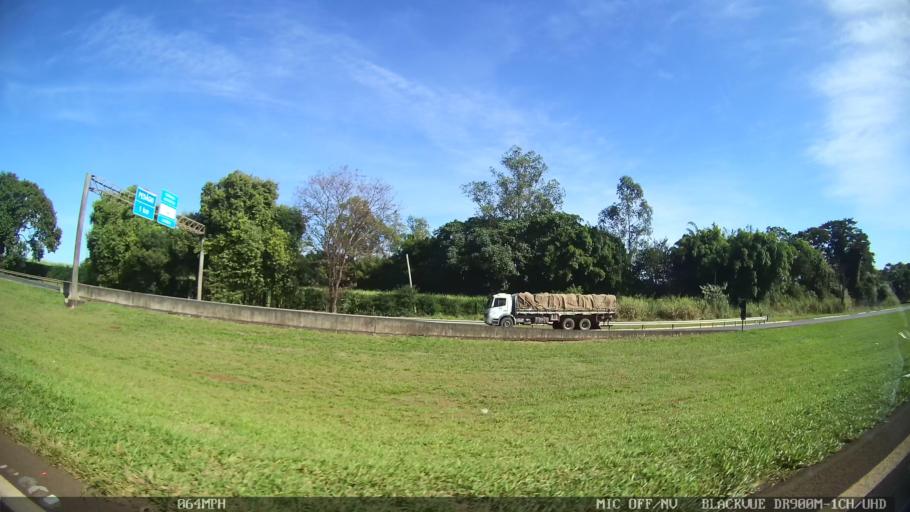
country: BR
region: Sao Paulo
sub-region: Leme
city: Leme
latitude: -22.2379
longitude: -47.3907
